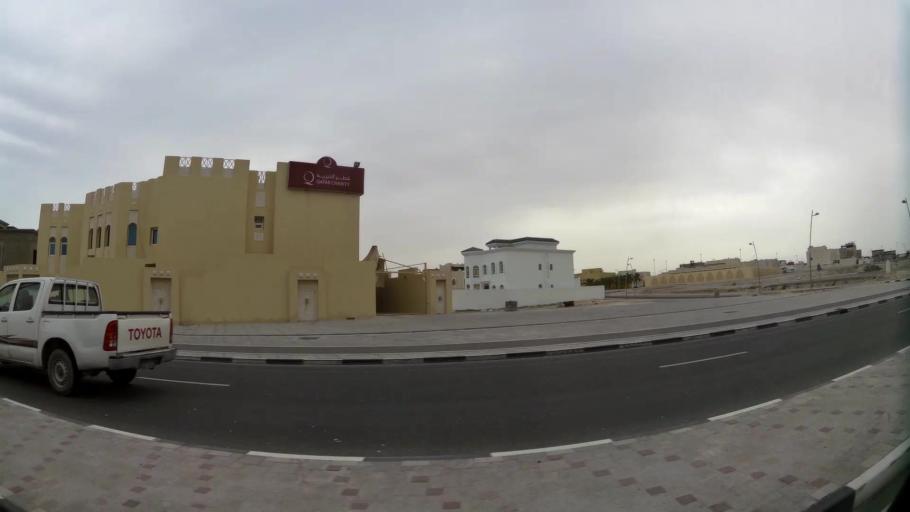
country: QA
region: Baladiyat ad Dawhah
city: Doha
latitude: 25.3448
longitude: 51.4898
